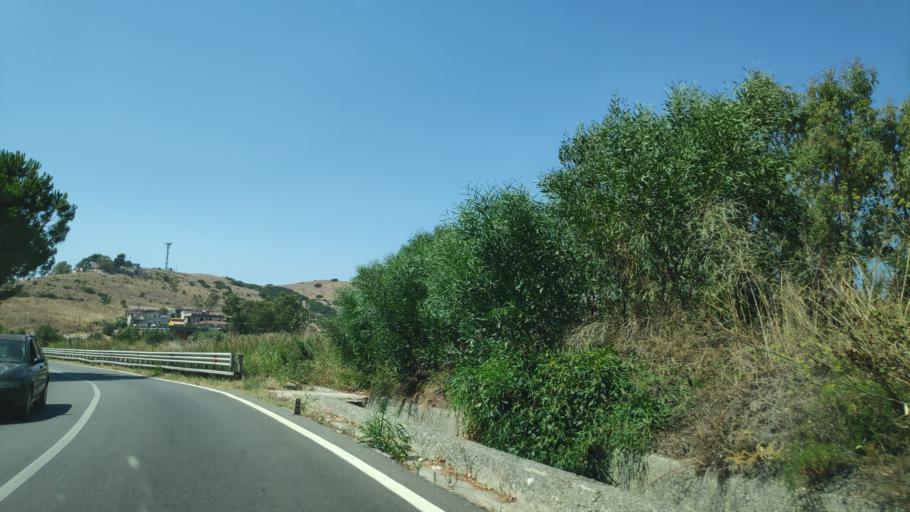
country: IT
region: Calabria
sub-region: Provincia di Reggio Calabria
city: Africo Nuovo
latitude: 38.0201
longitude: 16.1346
